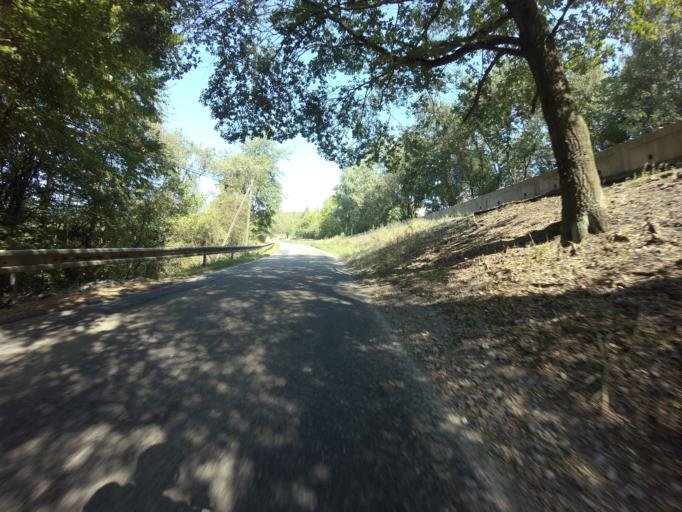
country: CZ
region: Central Bohemia
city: Kamenny Privoz
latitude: 49.8602
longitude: 14.5415
